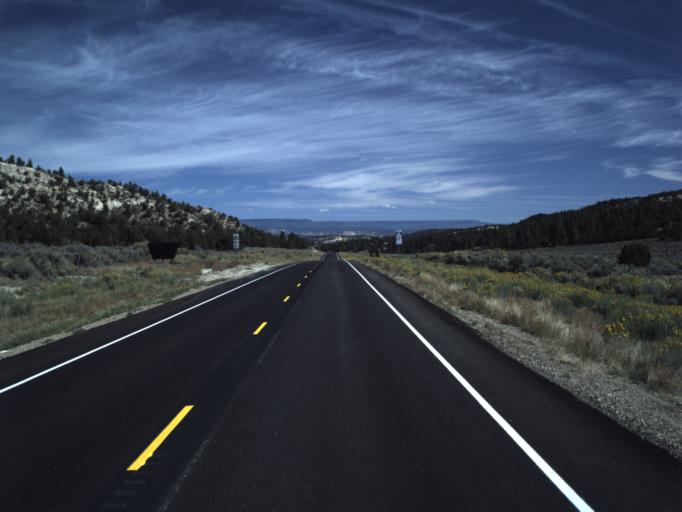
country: US
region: Utah
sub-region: Garfield County
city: Panguitch
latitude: 37.6503
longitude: -111.8427
